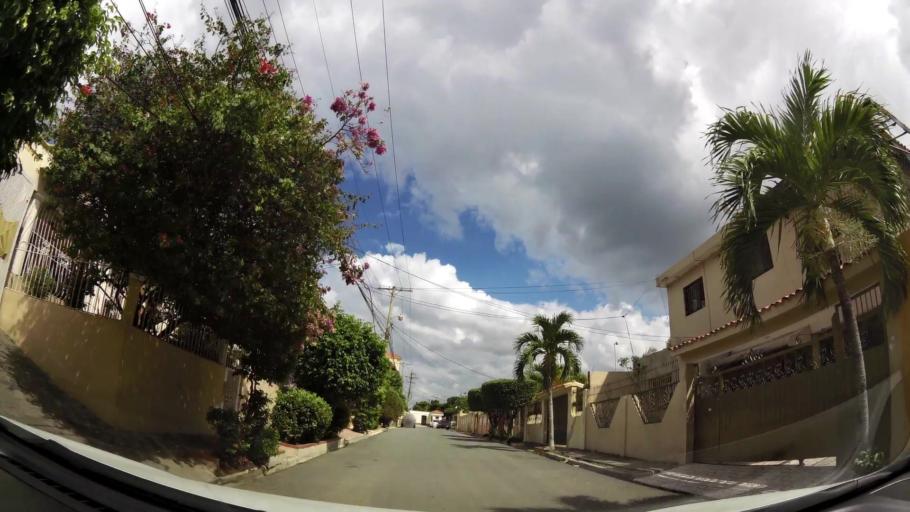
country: DO
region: Nacional
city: Ensanche Luperon
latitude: 18.5375
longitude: -69.9044
